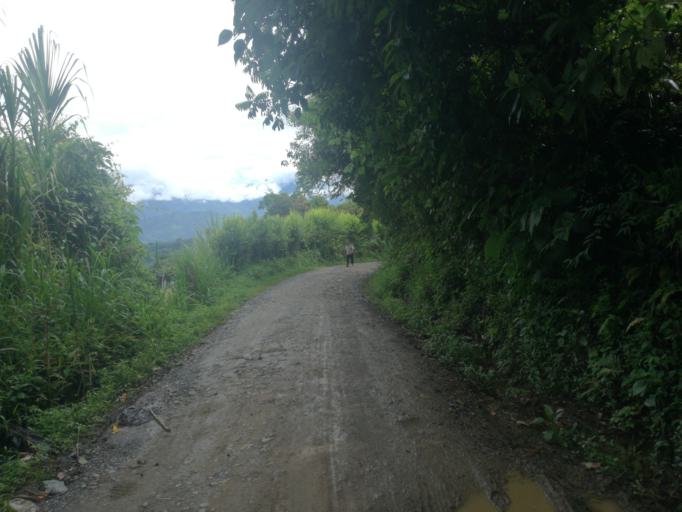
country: CO
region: Boyaca
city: Santana
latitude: 6.0615
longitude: -73.4835
